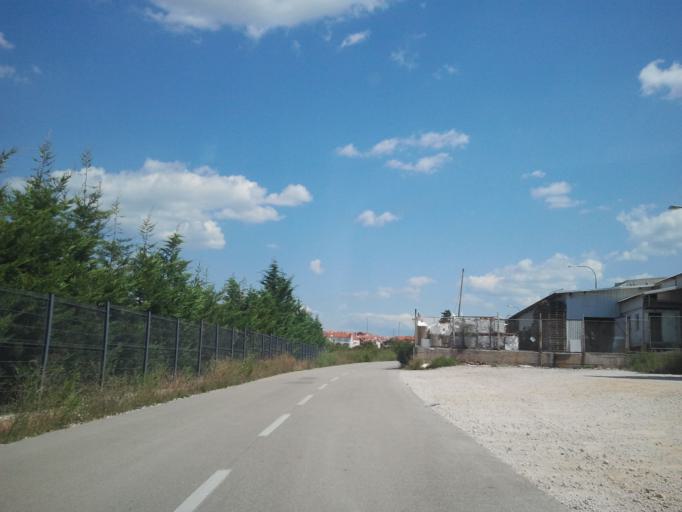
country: HR
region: Zadarska
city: Zadar
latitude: 44.1062
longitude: 15.2587
